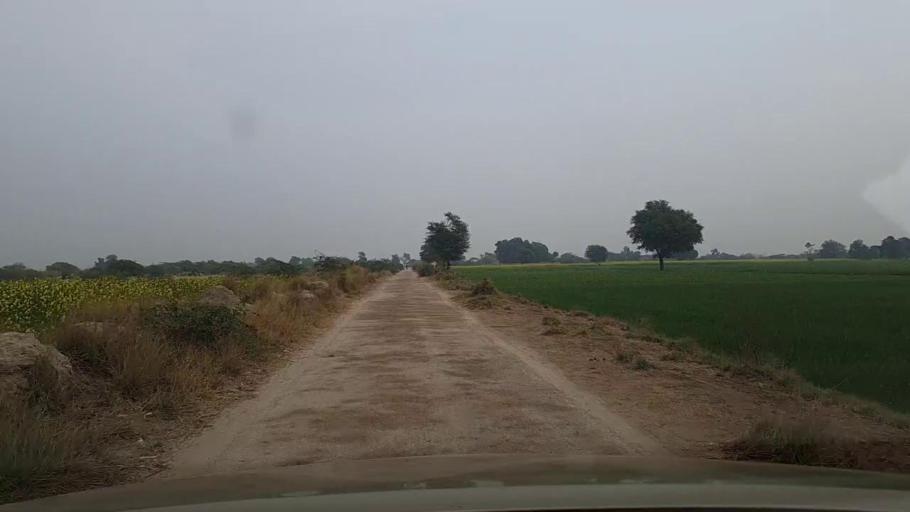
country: PK
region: Sindh
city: Sanghar
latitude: 26.1132
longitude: 68.9078
